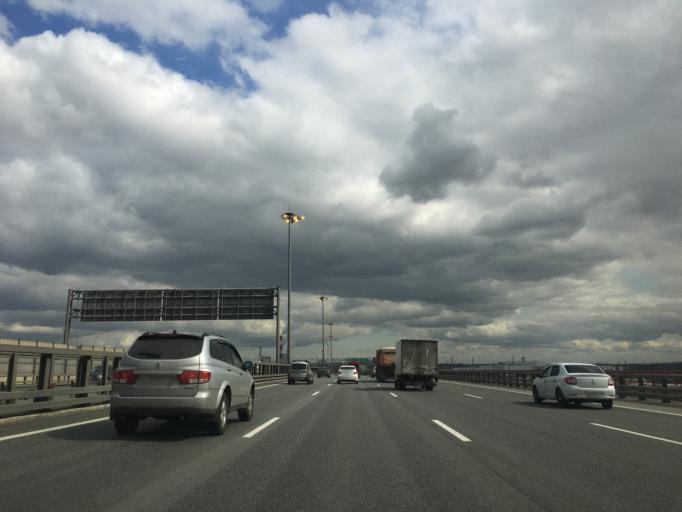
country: RU
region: St.-Petersburg
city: Shushary
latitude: 59.8174
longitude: 30.3955
